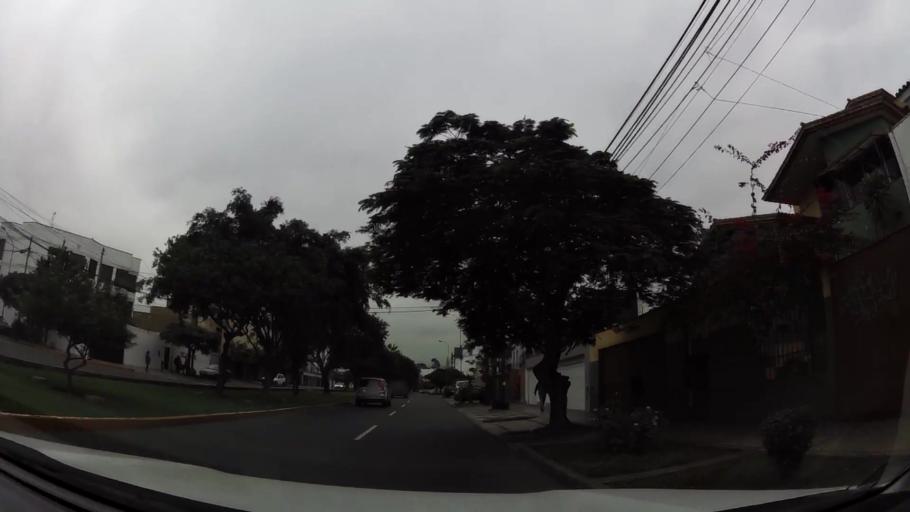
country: PE
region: Lima
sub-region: Lima
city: Surco
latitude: -12.1209
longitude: -76.9951
